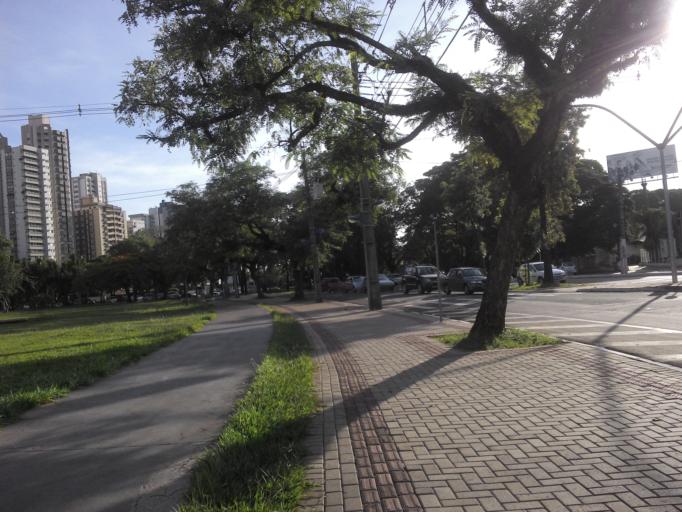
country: BR
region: Parana
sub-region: Maringa
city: Maringa
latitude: -23.4273
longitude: -51.9378
